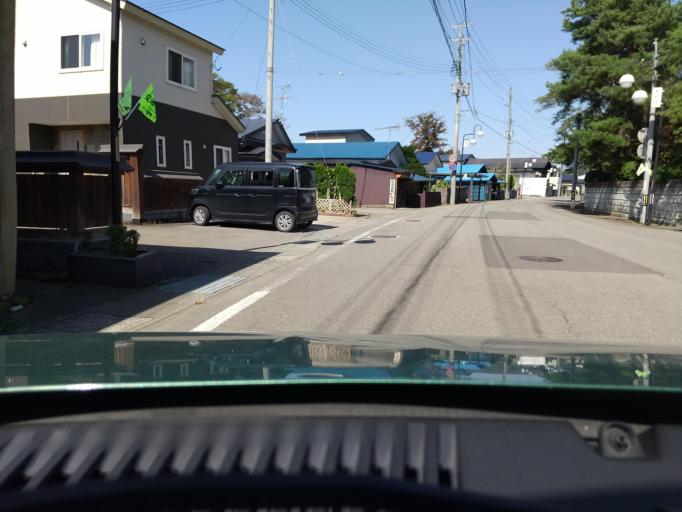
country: JP
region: Akita
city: Omagari
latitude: 39.6125
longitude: 140.3222
